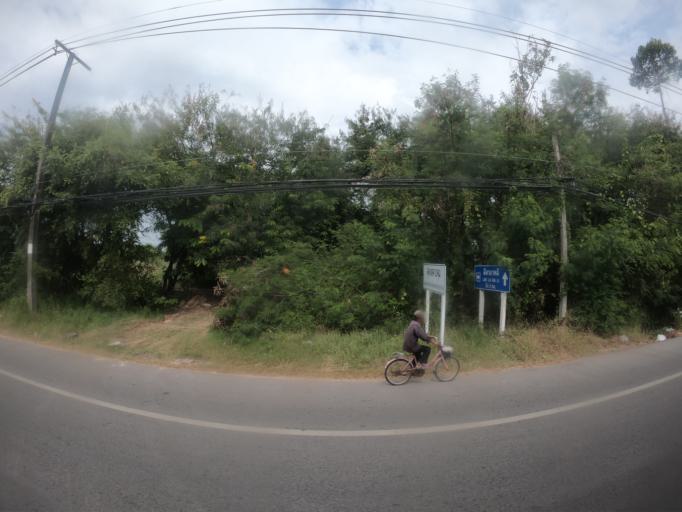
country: TH
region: Roi Et
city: Roi Et
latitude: 16.0615
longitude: 103.6245
